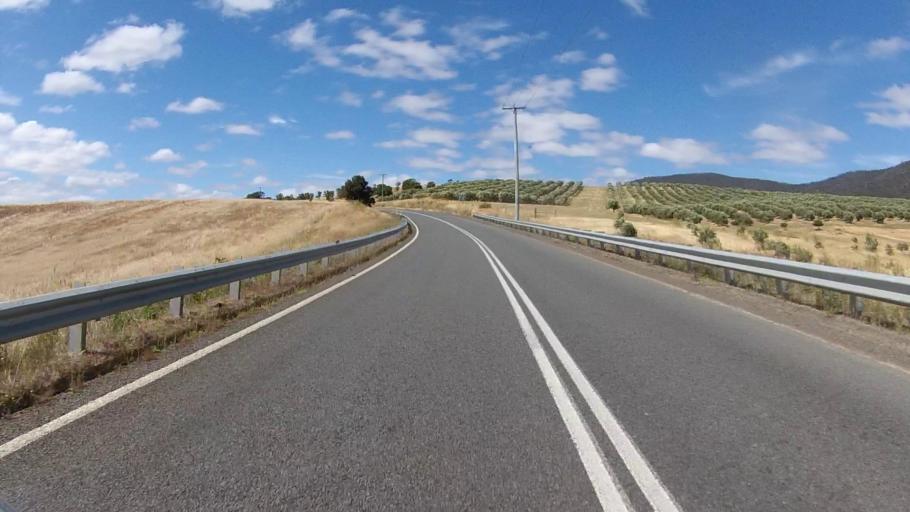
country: AU
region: Tasmania
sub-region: Brighton
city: Old Beach
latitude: -42.6033
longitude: 147.4170
